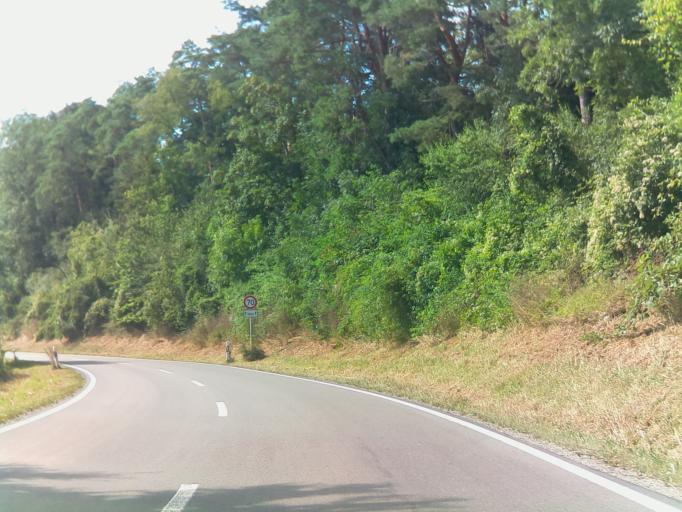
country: DE
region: Baden-Wuerttemberg
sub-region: Karlsruhe Region
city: Ostringen
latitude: 49.1841
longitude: 8.7340
